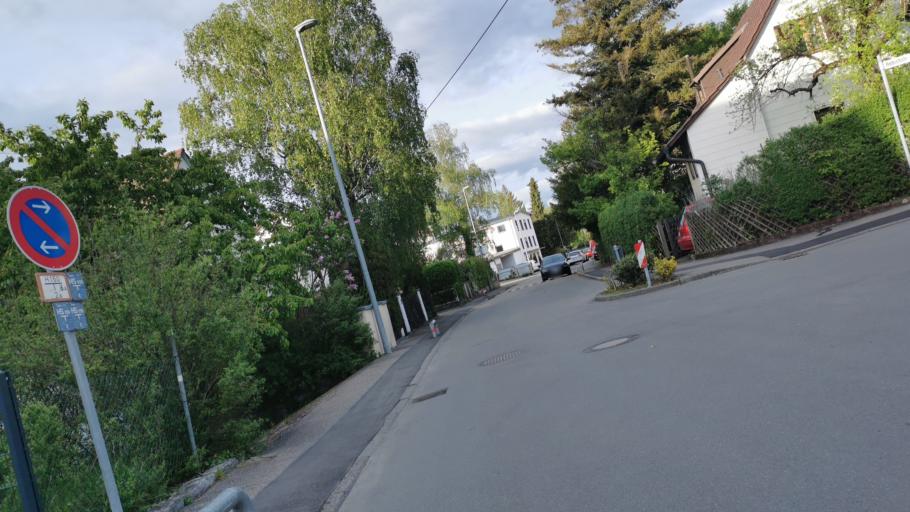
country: DE
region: Baden-Wuerttemberg
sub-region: Regierungsbezirk Stuttgart
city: Korntal
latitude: 48.8273
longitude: 9.1266
